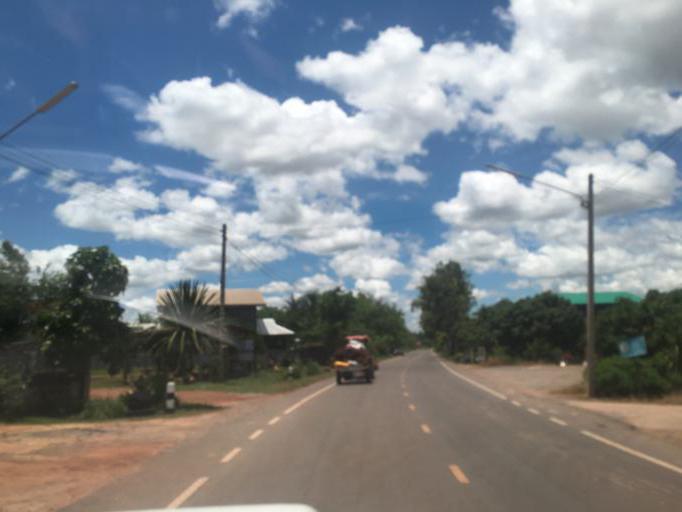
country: TH
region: Changwat Udon Thani
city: Nong Saeng
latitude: 17.1760
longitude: 102.7731
